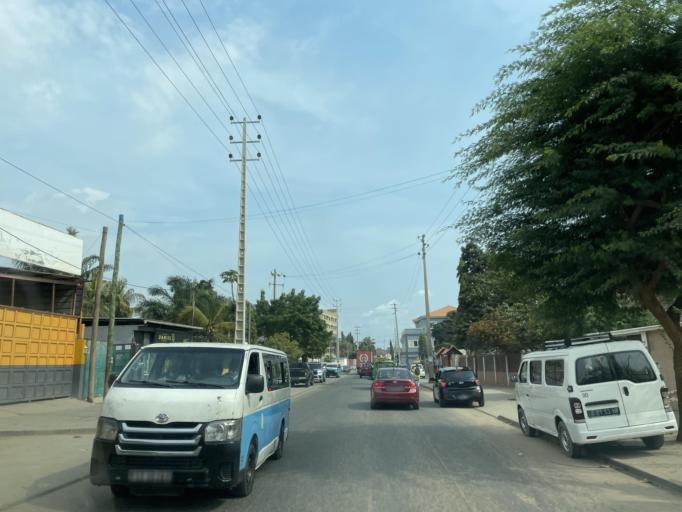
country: AO
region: Luanda
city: Luanda
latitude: -8.8993
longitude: 13.1918
